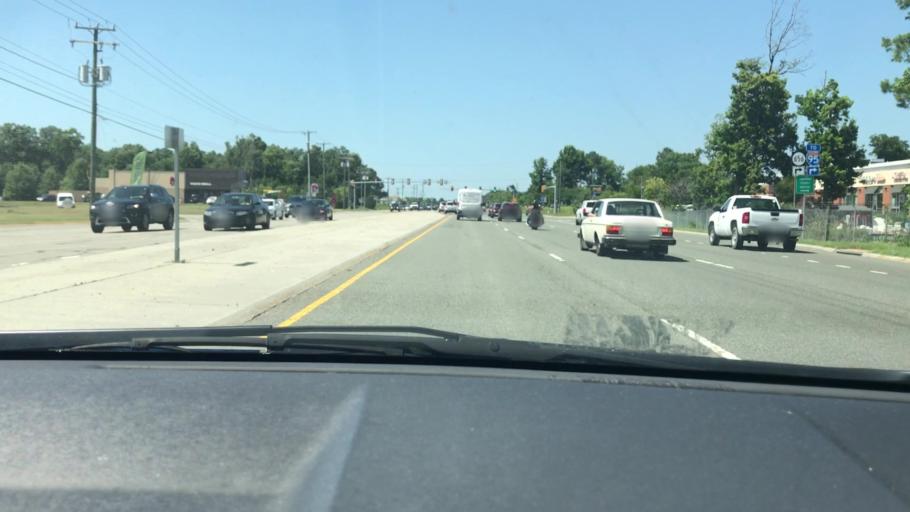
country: US
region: Virginia
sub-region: Henrico County
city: Glen Allen
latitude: 37.6850
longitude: -77.4621
